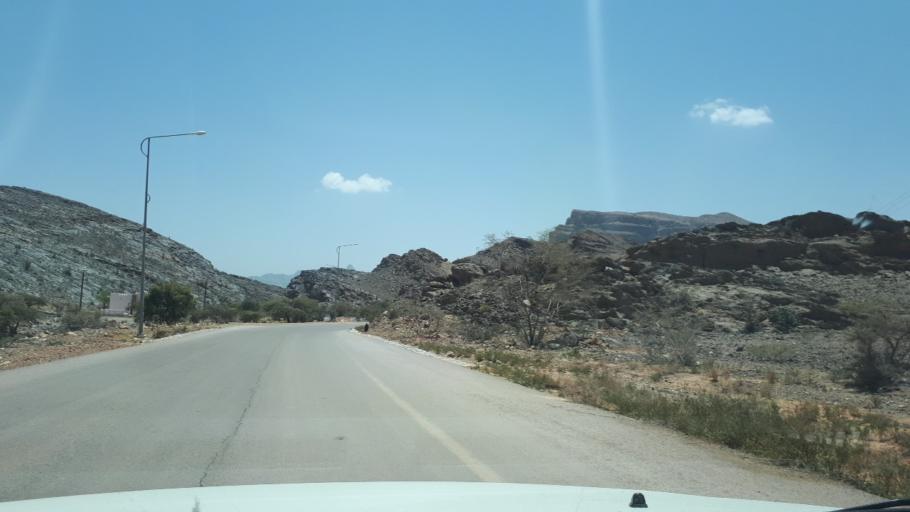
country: OM
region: Muhafazat ad Dakhiliyah
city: Bahla'
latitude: 23.2396
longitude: 57.1500
